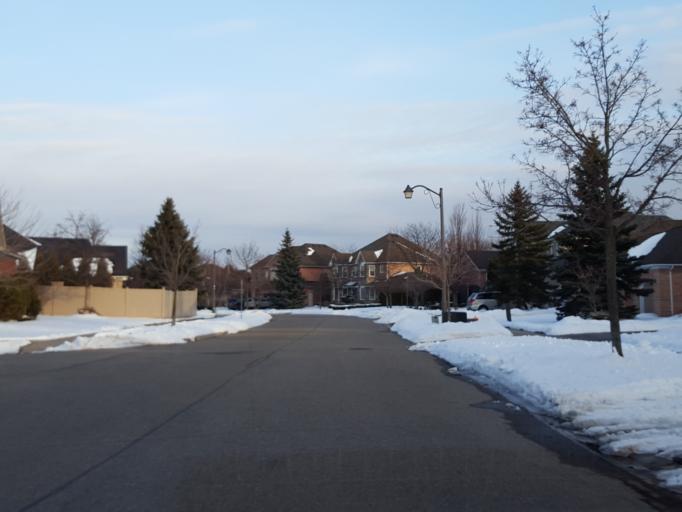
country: CA
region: Ontario
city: Burlington
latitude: 43.3930
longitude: -79.8031
